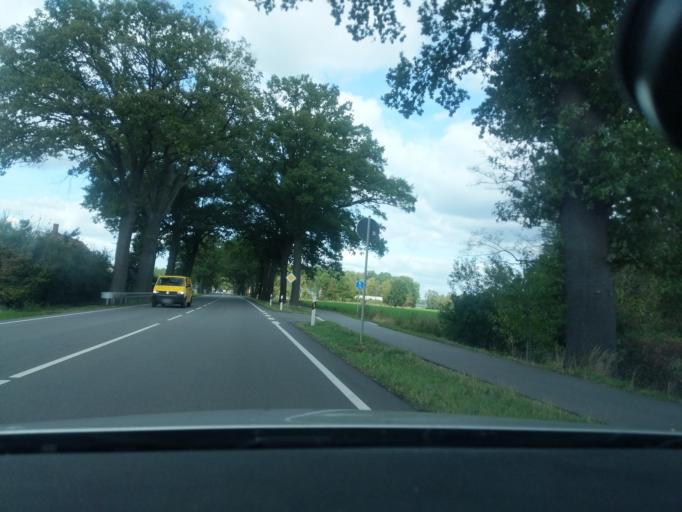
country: DE
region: Lower Saxony
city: Bohmte
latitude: 52.3830
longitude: 8.3110
